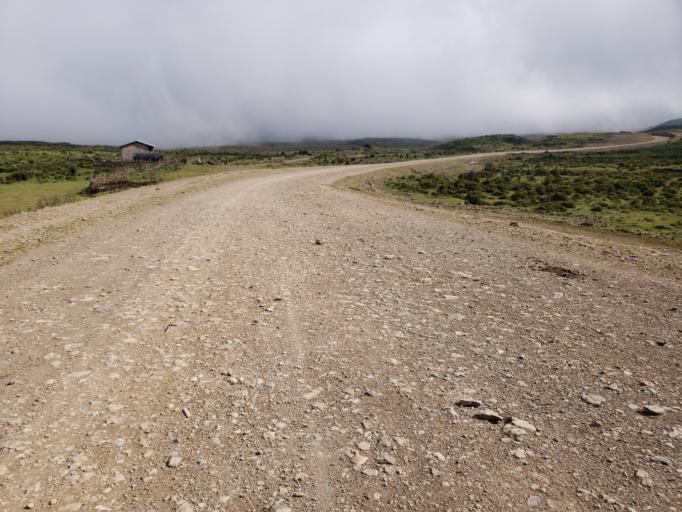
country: ET
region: Oromiya
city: Dodola
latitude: 6.7464
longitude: 39.4279
